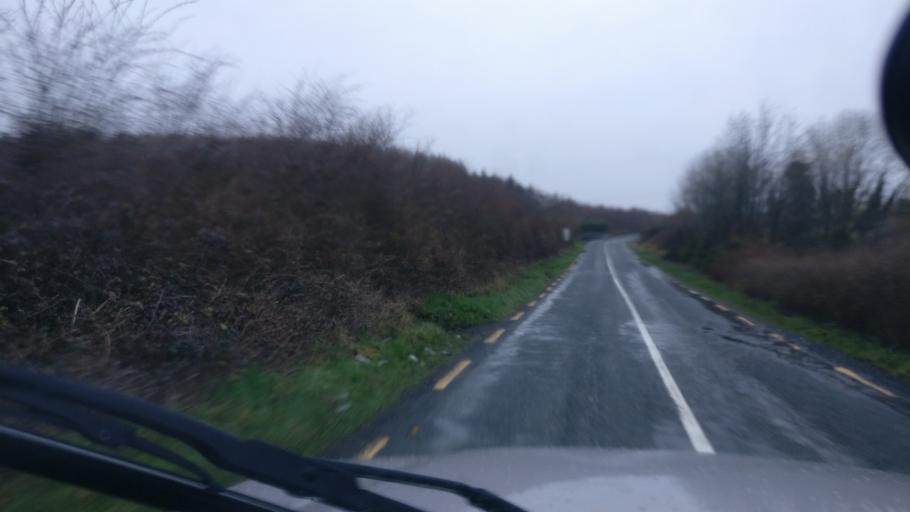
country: IE
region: Connaught
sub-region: County Galway
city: Loughrea
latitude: 53.1208
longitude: -8.4470
